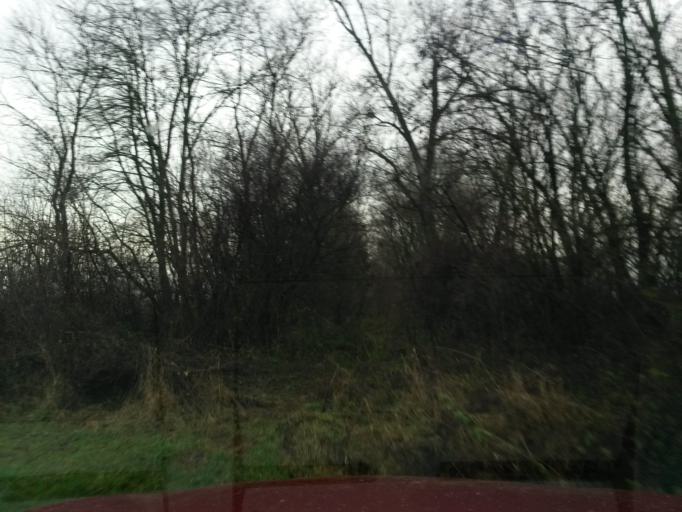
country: SK
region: Kosicky
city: Sobrance
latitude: 48.6412
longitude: 22.0772
